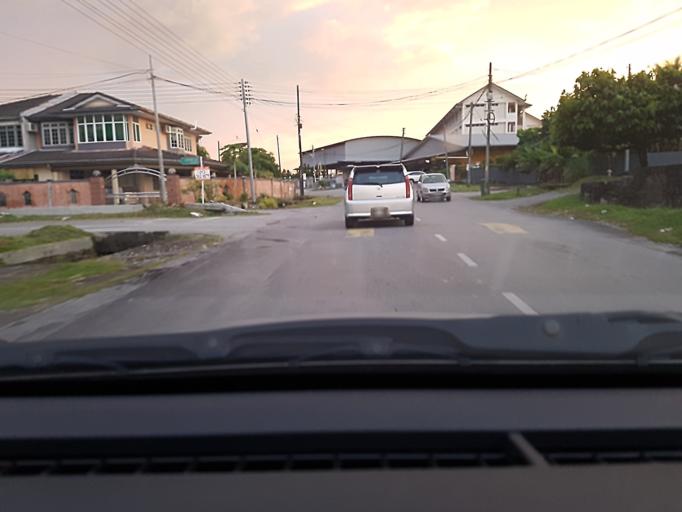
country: MY
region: Sarawak
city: Kuching
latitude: 1.4900
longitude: 110.3211
